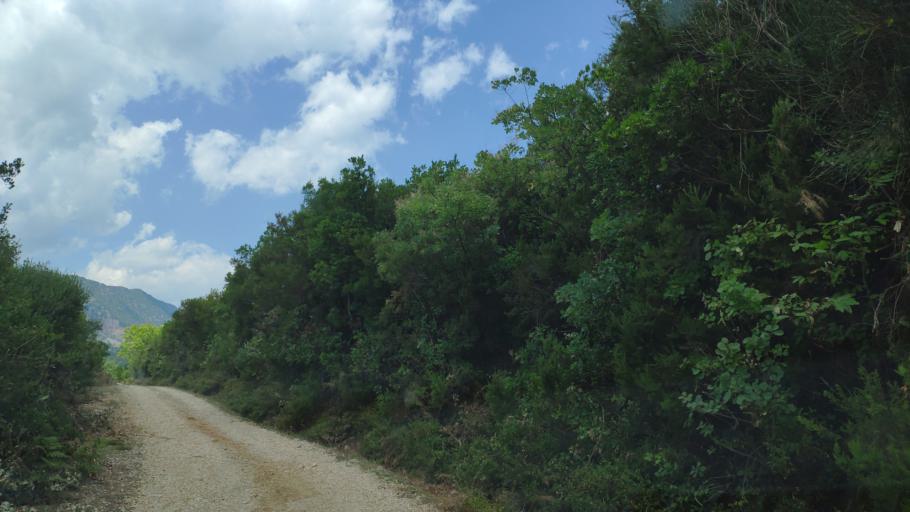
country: GR
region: Epirus
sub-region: Nomos Artas
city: Agios Dimitrios
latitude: 39.3175
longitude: 21.0109
